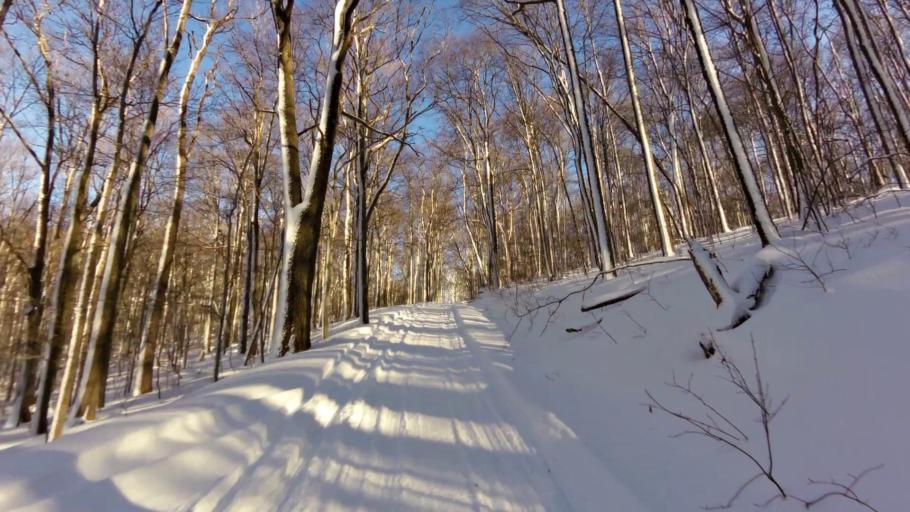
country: US
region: New York
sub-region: Cattaraugus County
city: Salamanca
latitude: 42.0734
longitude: -78.6916
